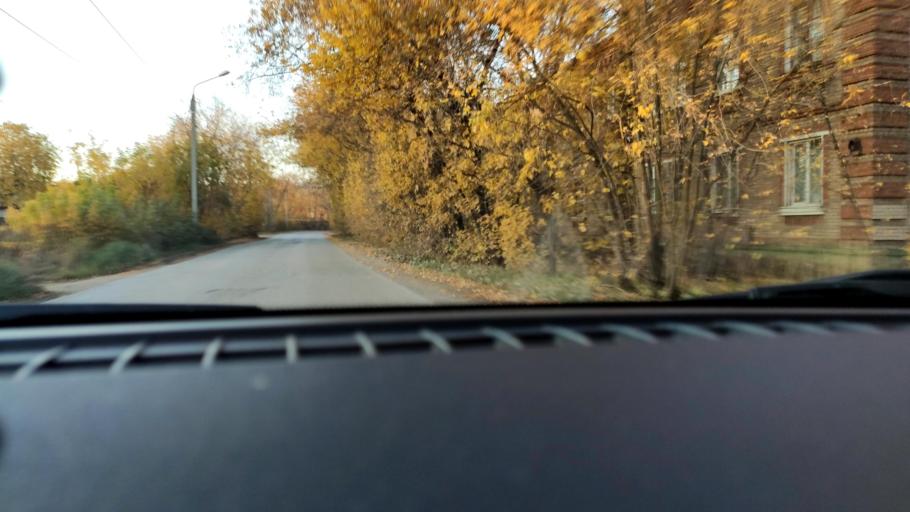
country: RU
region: Perm
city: Perm
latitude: 57.9703
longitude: 56.2765
